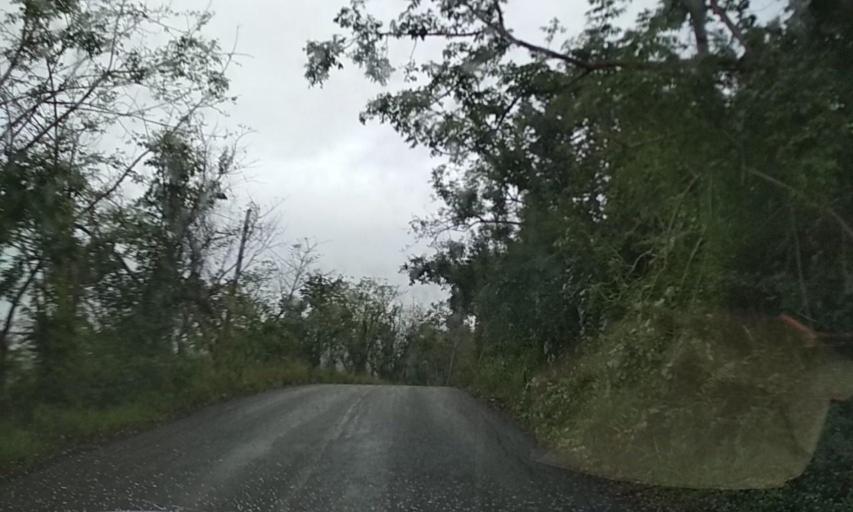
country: MX
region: Veracruz
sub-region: Coatzintla
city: Manuel Maria Contreras
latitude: 20.4553
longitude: -97.4739
